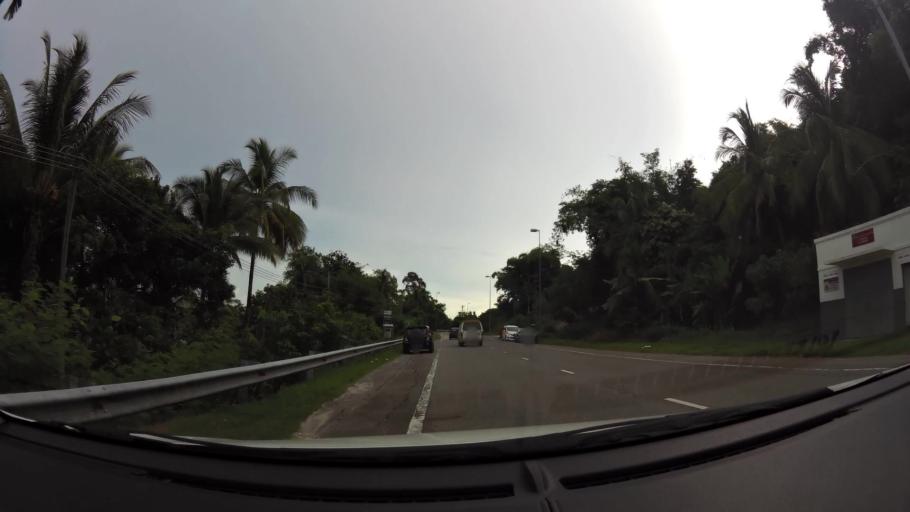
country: BN
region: Brunei and Muara
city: Bandar Seri Begawan
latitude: 4.8994
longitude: 114.9873
